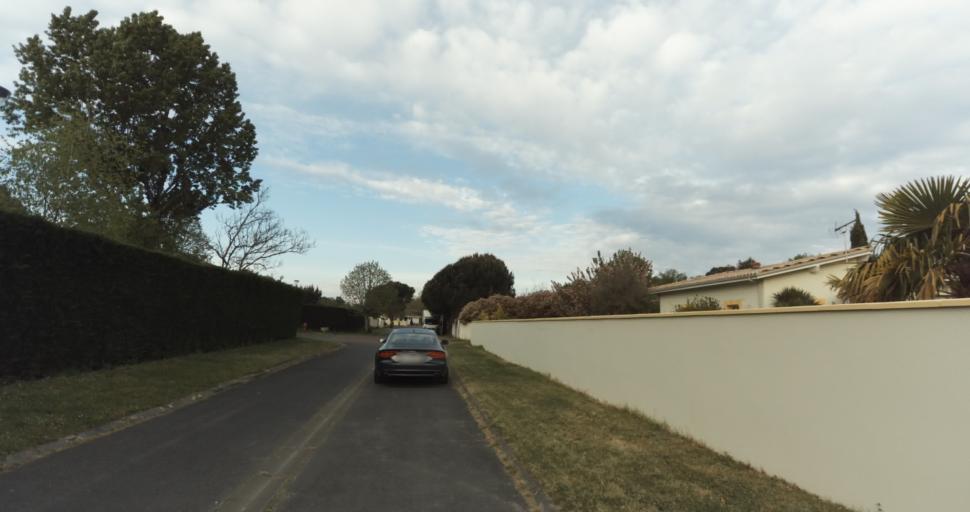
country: FR
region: Aquitaine
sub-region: Departement de la Gironde
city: Saint-Aubin-de-Medoc
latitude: 44.7753
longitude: -0.7367
